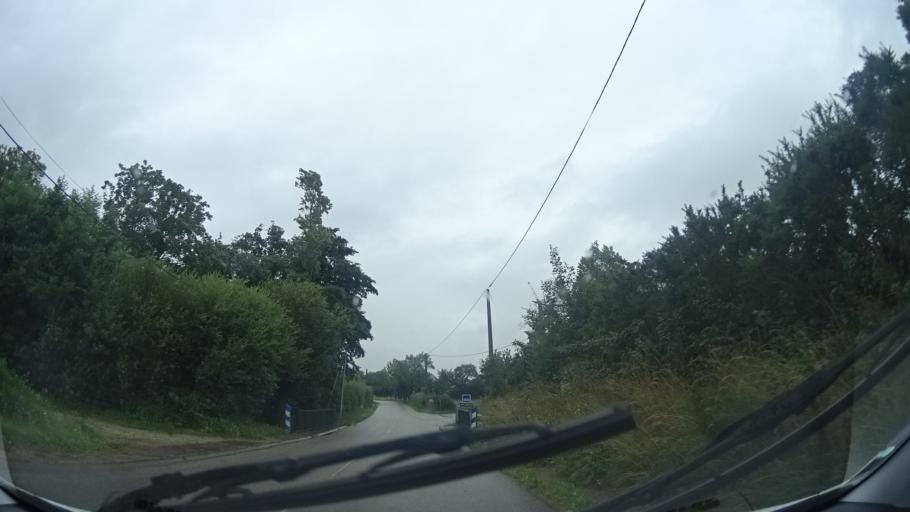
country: FR
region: Lower Normandy
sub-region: Departement de la Manche
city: Urville-Nacqueville
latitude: 49.5964
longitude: -1.7552
